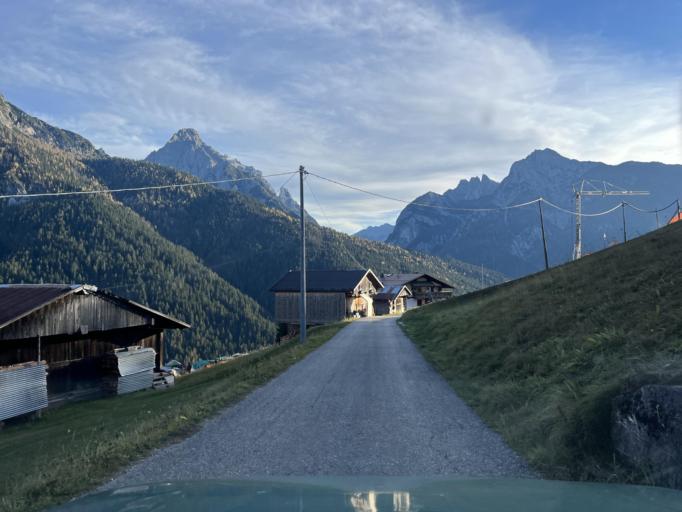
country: IT
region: Veneto
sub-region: Provincia di Belluno
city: San Pietro di Cadore
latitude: 46.5794
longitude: 12.5961
